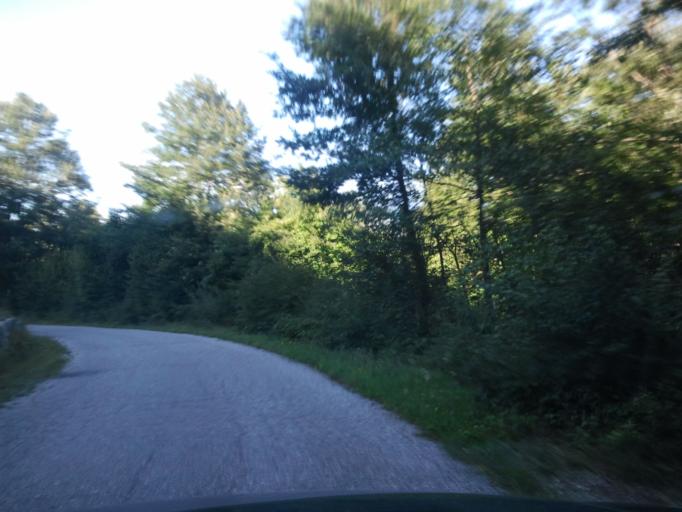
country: HR
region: Zadarska
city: Obrovac
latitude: 44.3379
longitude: 15.6443
